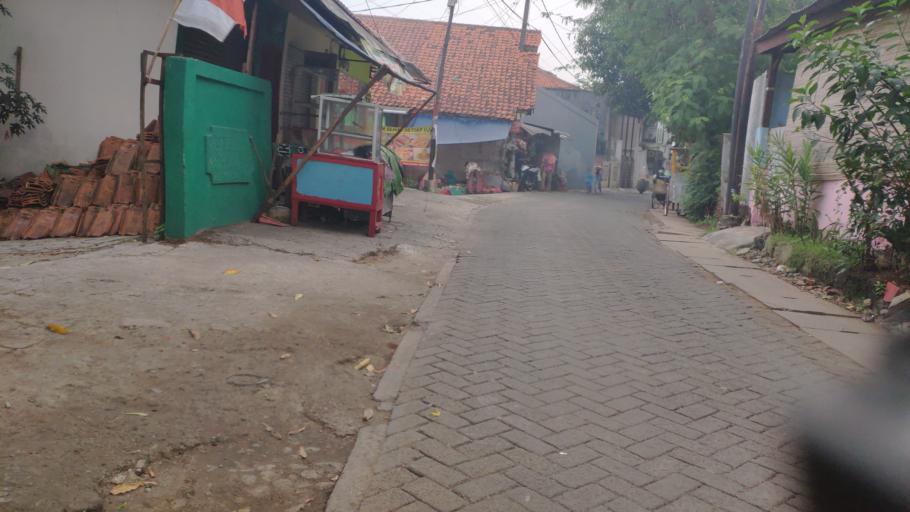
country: ID
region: West Java
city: Depok
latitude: -6.3144
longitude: 106.8274
